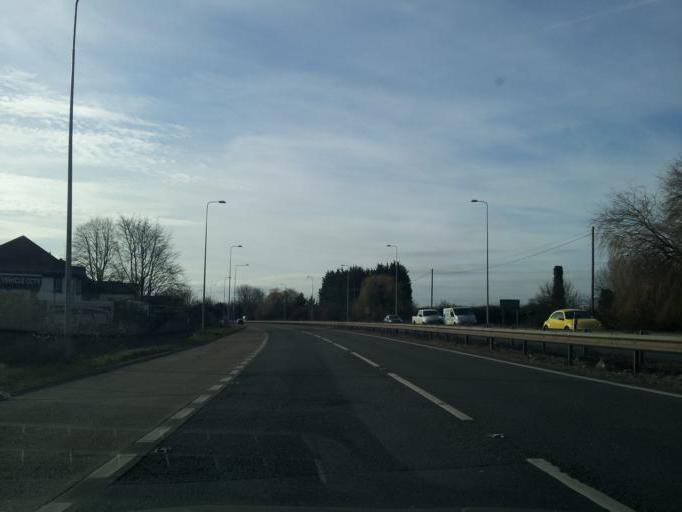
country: GB
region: England
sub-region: Central Bedfordshire
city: Sandy
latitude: 52.1325
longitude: -0.3005
